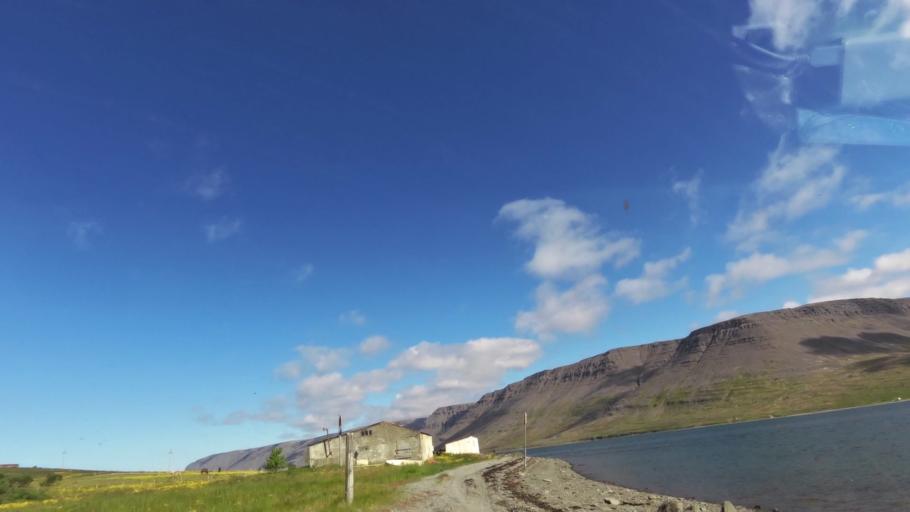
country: IS
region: West
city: Olafsvik
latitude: 65.6206
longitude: -23.8680
